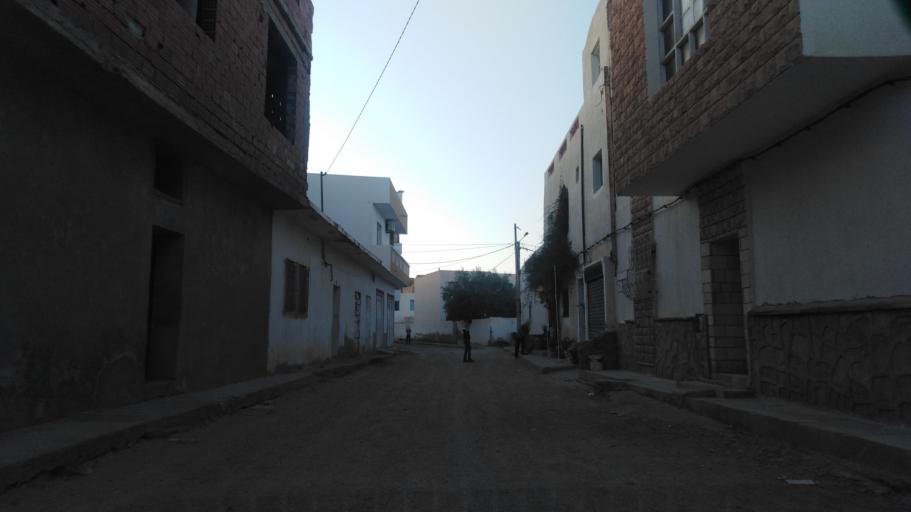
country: TN
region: Tataouine
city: Tataouine
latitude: 32.9385
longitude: 10.4570
